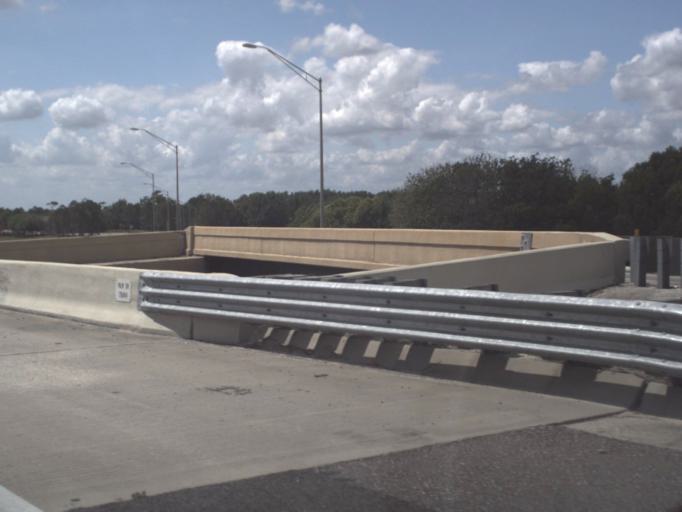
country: US
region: Florida
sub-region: Orange County
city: Ocoee
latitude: 28.5771
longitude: -81.5573
